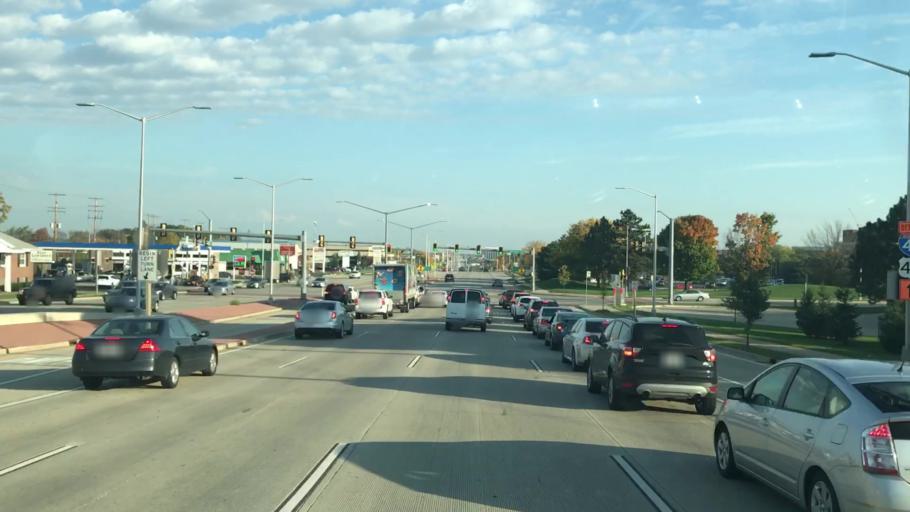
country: US
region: Wisconsin
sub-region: Waukesha County
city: Elm Grove
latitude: 43.0374
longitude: -88.0470
